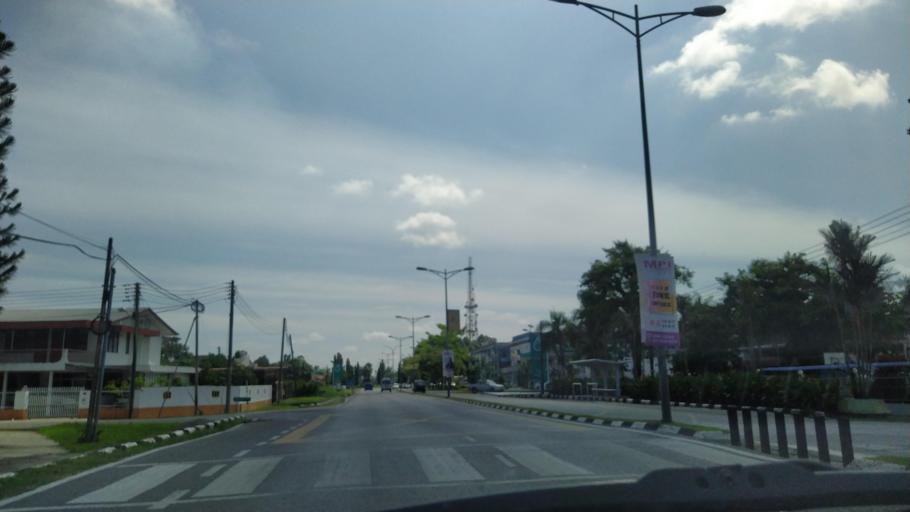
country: MY
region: Sarawak
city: Sibu
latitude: 2.3096
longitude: 111.8297
